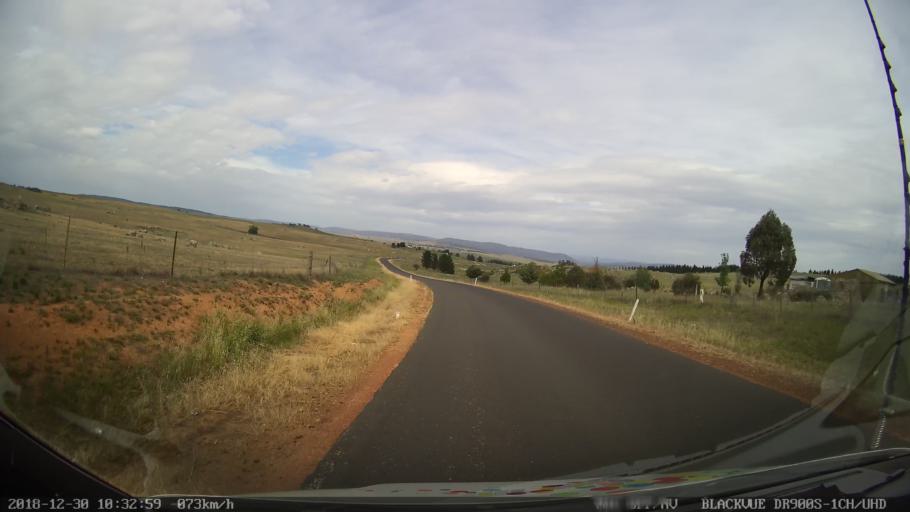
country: AU
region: New South Wales
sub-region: Snowy River
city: Berridale
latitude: -36.4986
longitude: 148.8587
